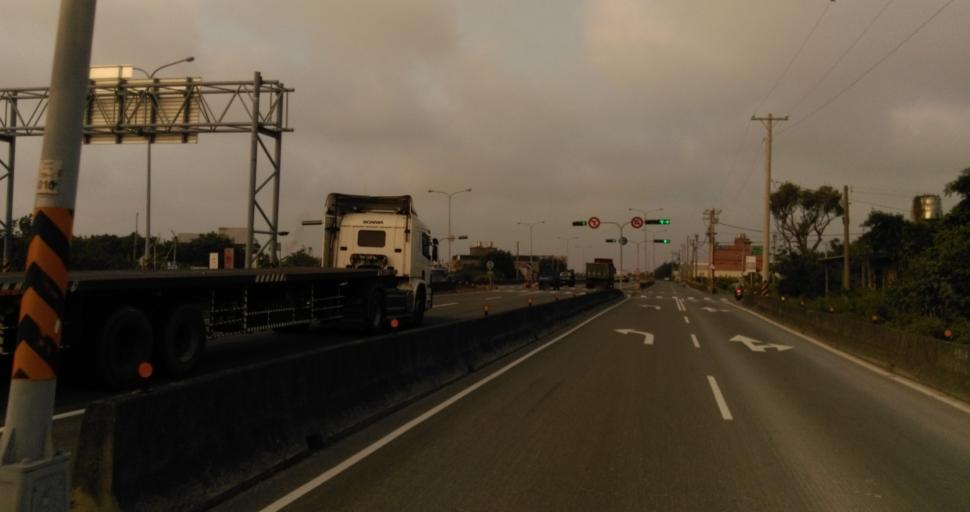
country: TW
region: Taiwan
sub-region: Hsinchu
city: Hsinchu
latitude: 24.7849
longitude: 120.9164
